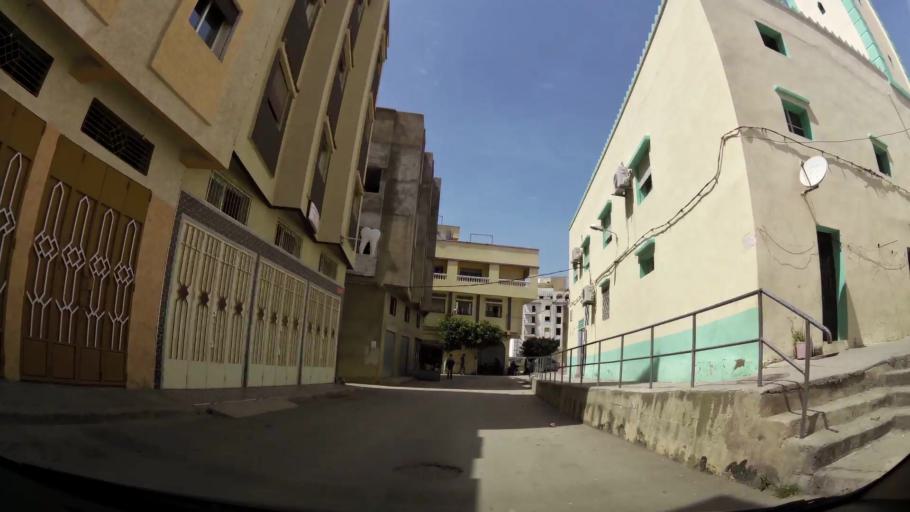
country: MA
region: Tanger-Tetouan
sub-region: Tanger-Assilah
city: Tangier
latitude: 35.7534
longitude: -5.8472
